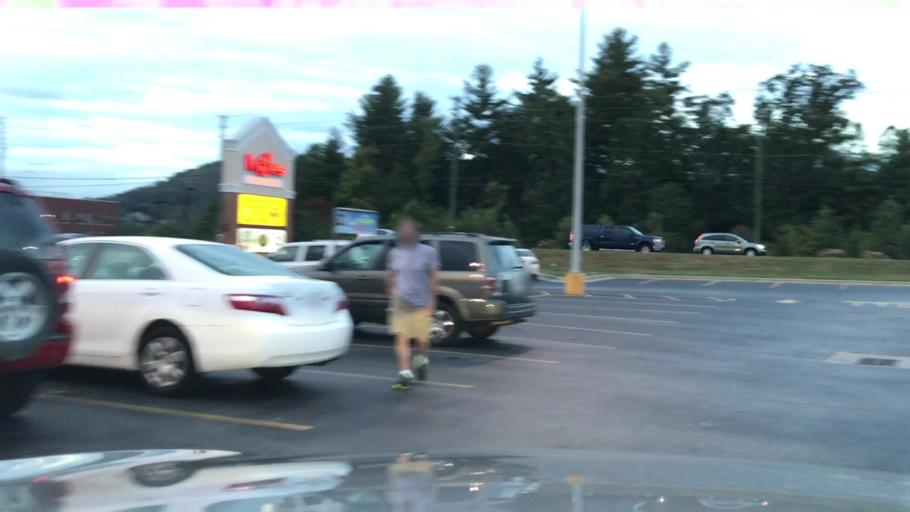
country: US
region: North Carolina
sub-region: Buncombe County
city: Royal Pines
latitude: 35.4798
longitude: -82.5492
